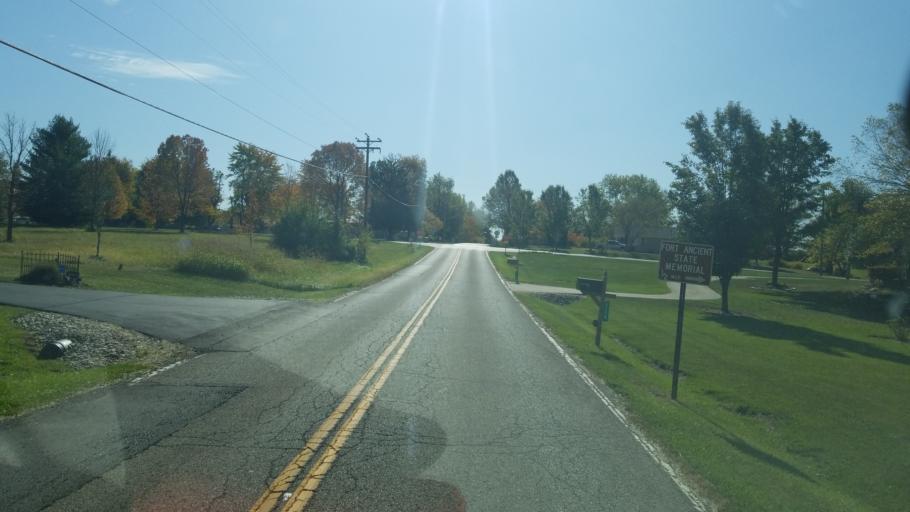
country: US
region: Ohio
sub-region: Warren County
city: Morrow
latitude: 39.4093
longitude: -84.0767
